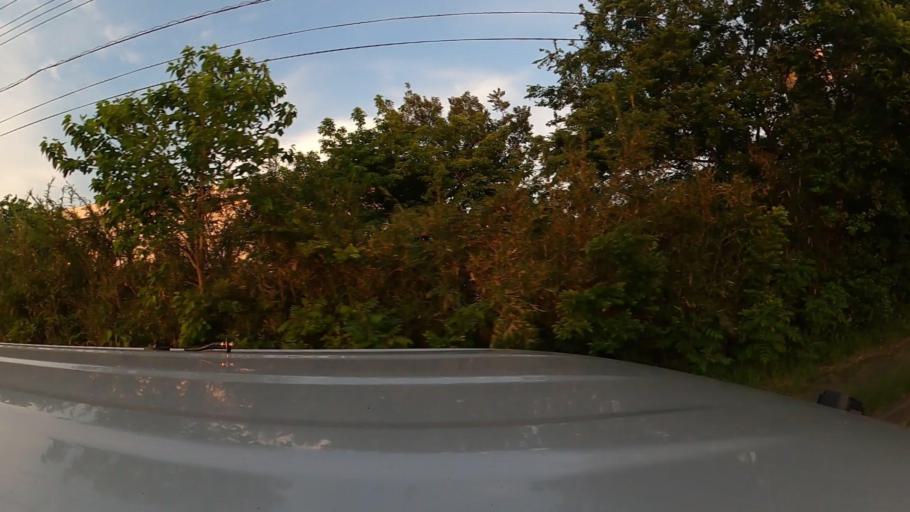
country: JP
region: Ibaraki
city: Ushiku
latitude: 36.0248
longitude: 140.0876
